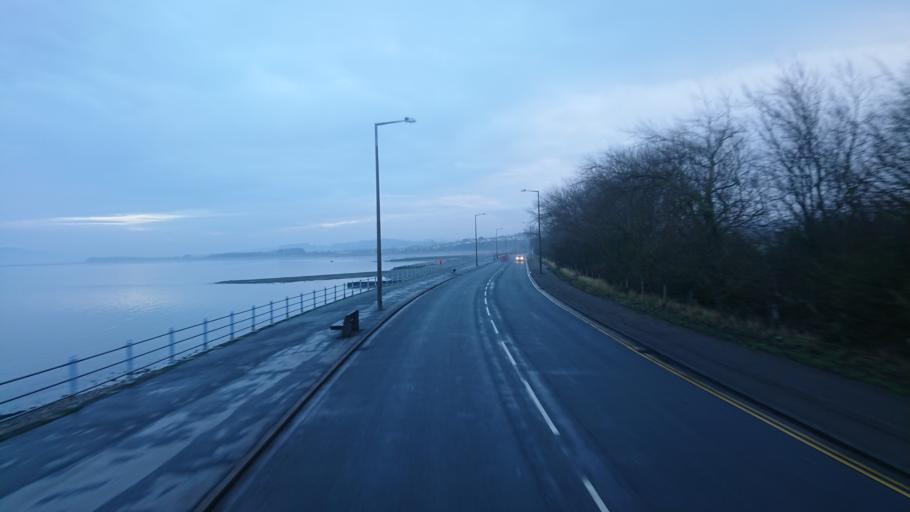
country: GB
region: England
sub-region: Lancashire
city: Morecambe
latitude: 54.0848
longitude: -2.8317
